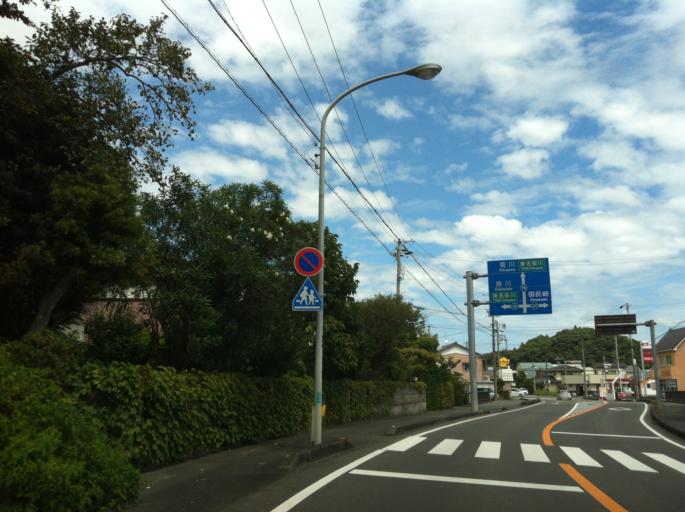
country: JP
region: Shizuoka
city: Kakegawa
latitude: 34.7155
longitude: 138.0470
